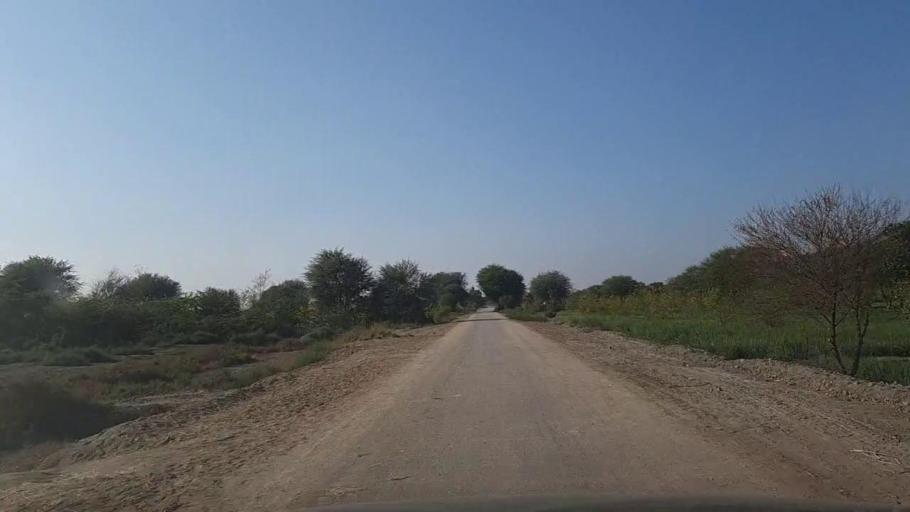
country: PK
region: Sindh
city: Digri
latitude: 25.0245
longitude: 69.2281
